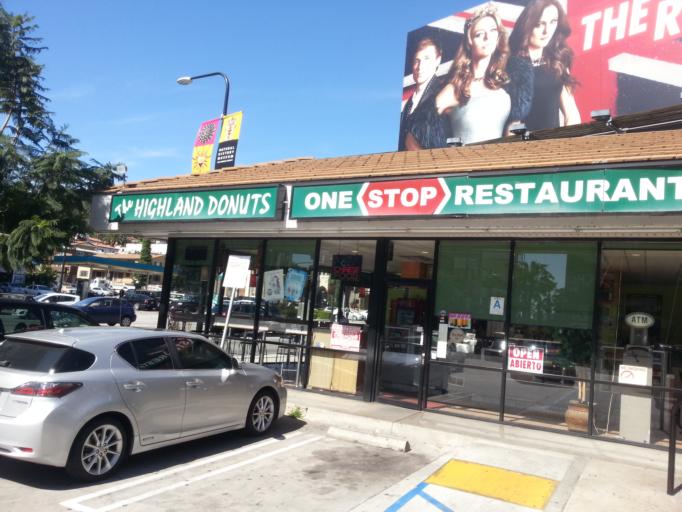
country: US
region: California
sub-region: Los Angeles County
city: Hollywood
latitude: 34.1035
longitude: -118.3384
